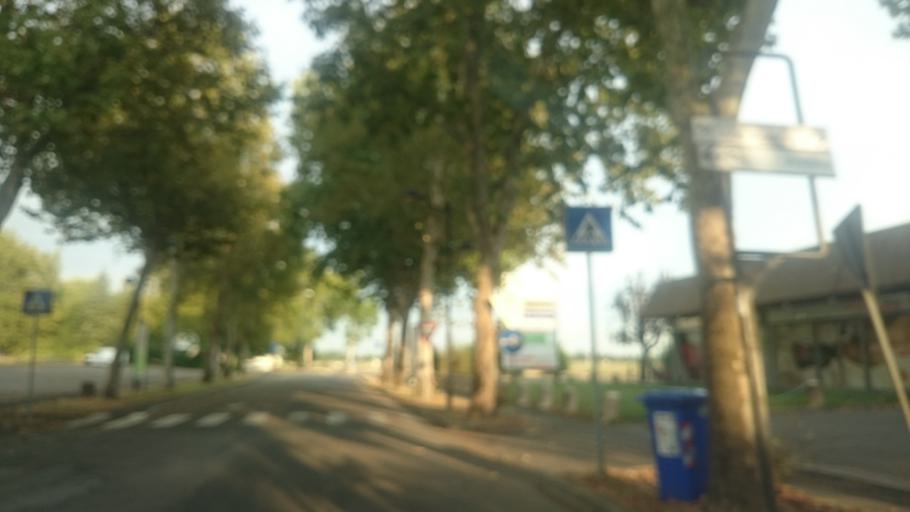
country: IT
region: Emilia-Romagna
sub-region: Provincia di Reggio Emilia
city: Reggio nell'Emilia
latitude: 44.7022
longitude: 10.6578
